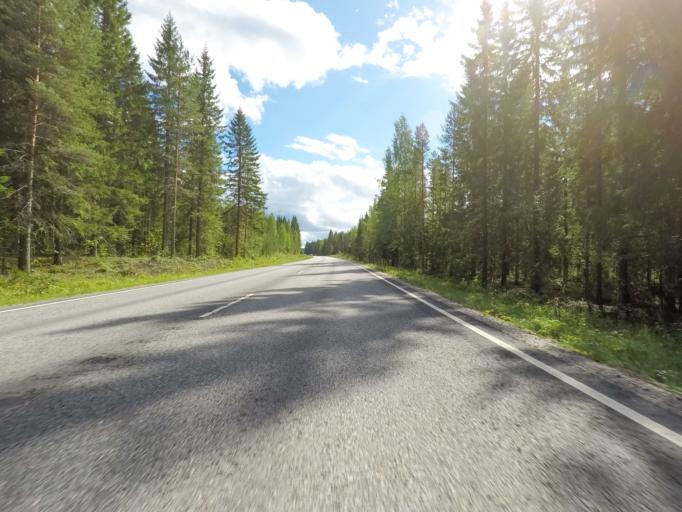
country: FI
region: Central Finland
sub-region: Jyvaeskylae
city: Toivakka
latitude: 62.2376
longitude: 26.1820
